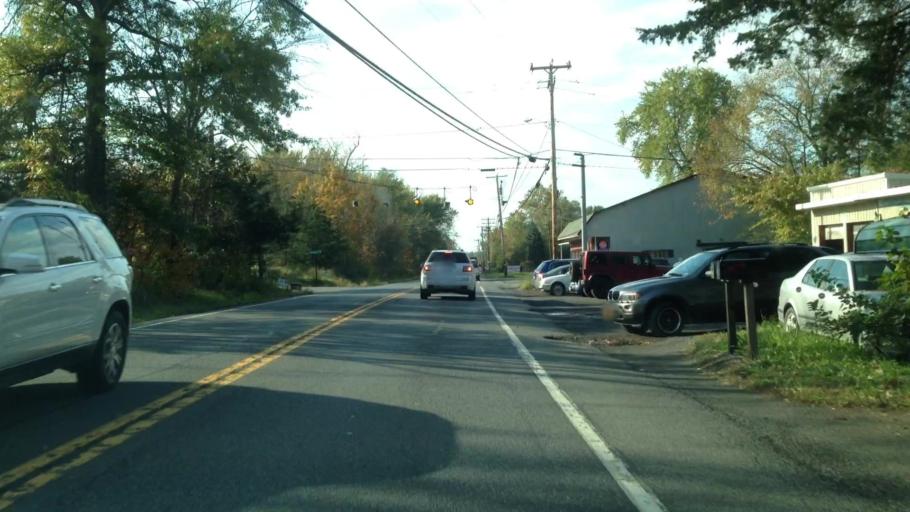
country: US
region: New York
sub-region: Ulster County
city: New Paltz
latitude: 41.7679
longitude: -74.0771
